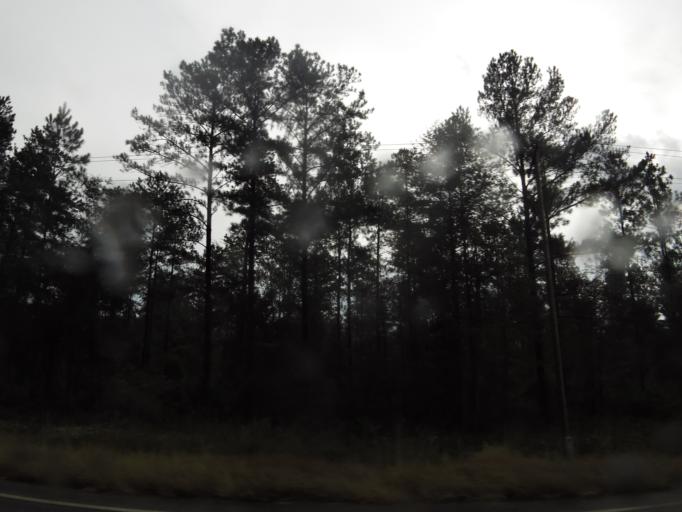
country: US
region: Georgia
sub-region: Wayne County
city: Jesup
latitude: 31.5758
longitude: -81.8823
